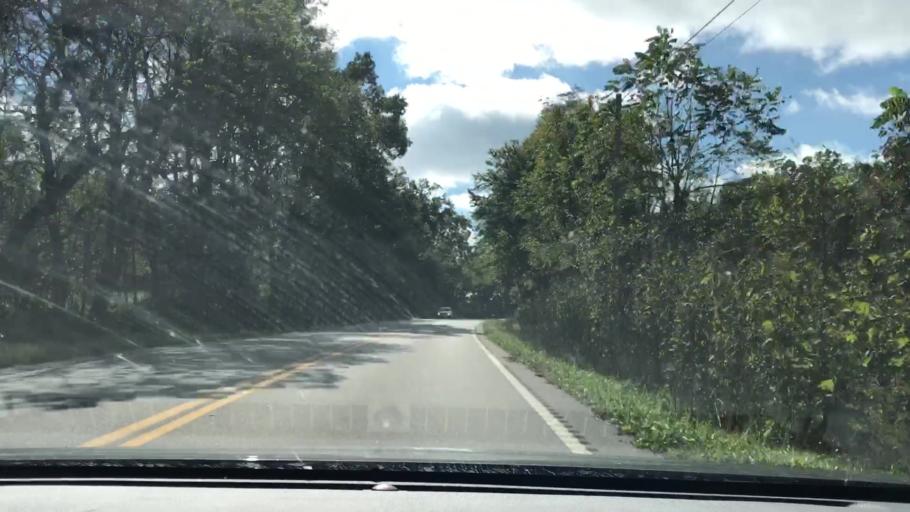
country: US
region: Tennessee
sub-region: Fentress County
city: Jamestown
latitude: 36.3712
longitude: -84.7880
